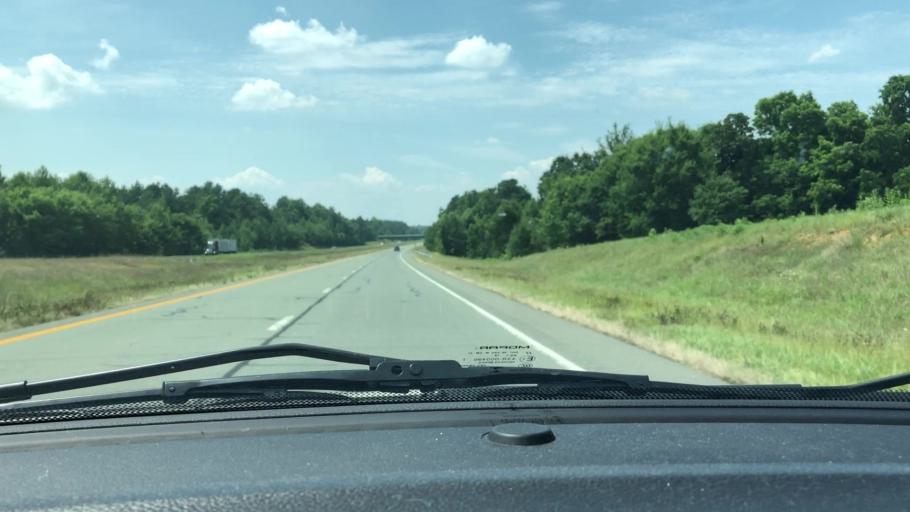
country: US
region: North Carolina
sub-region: Randolph County
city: Liberty
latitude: 35.7925
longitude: -79.5289
